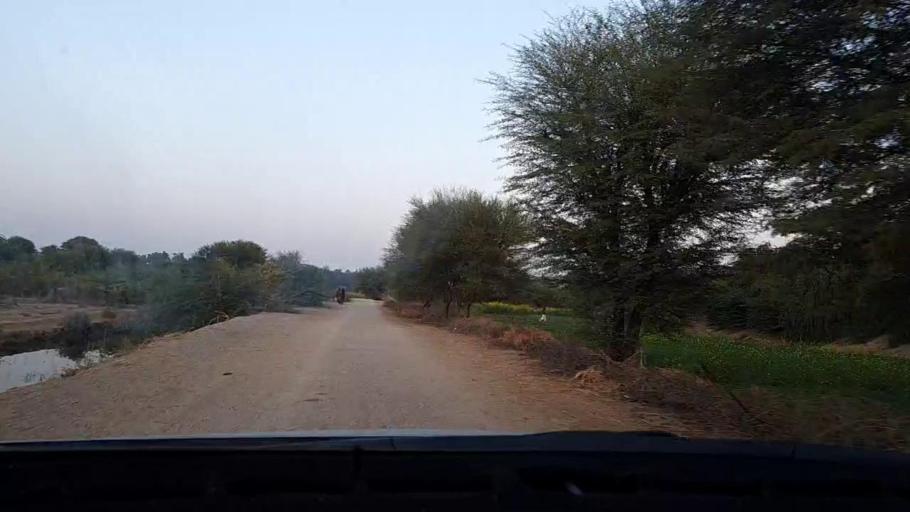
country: PK
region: Sindh
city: Tando Mittha Khan
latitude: 25.8579
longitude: 69.3123
